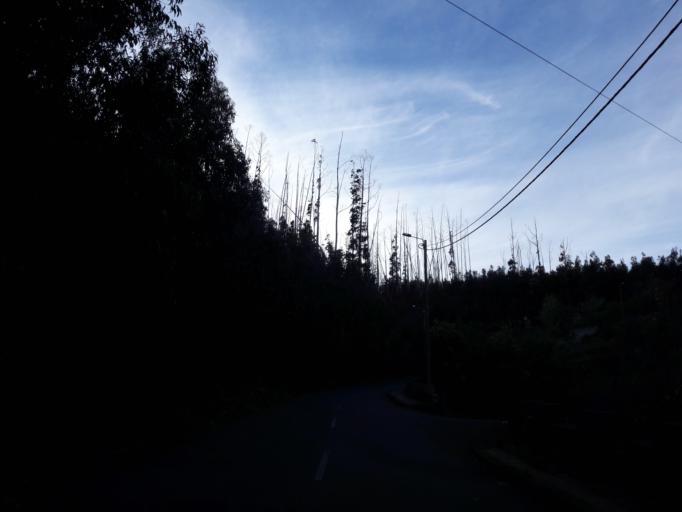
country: PT
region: Madeira
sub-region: Santa Cruz
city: Camacha
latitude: 32.6873
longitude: -16.8627
